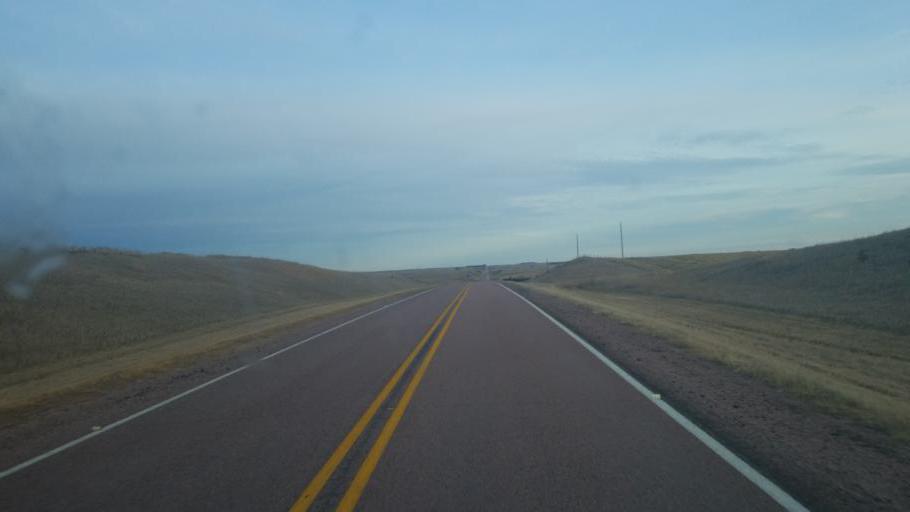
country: US
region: Nebraska
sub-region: Knox County
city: Center
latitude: 42.7276
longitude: -97.7772
